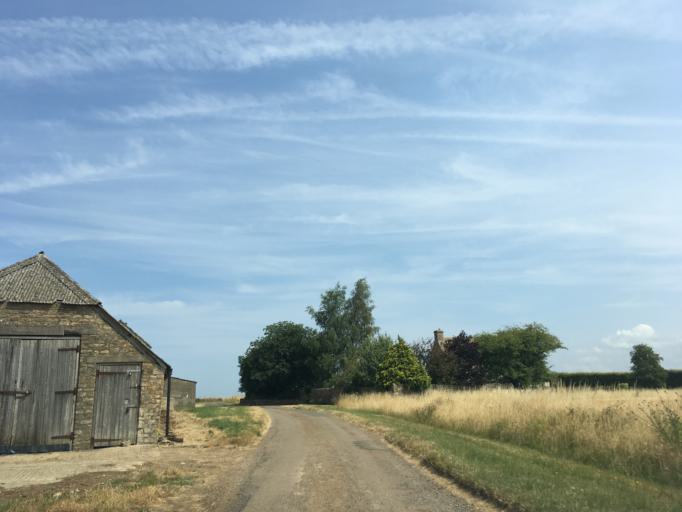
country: GB
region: England
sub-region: Gloucestershire
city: Nailsworth
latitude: 51.6616
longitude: -2.2426
